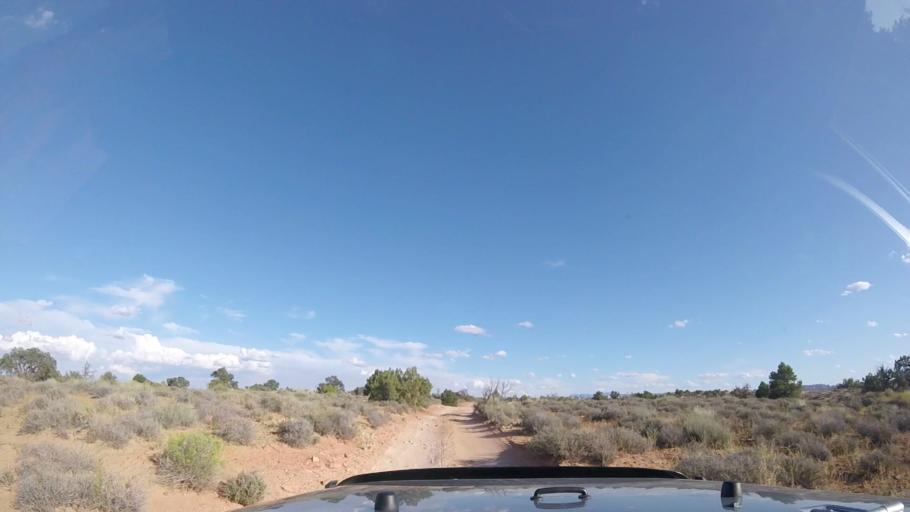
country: US
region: Utah
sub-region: Grand County
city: Moab
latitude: 38.2141
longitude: -109.8117
